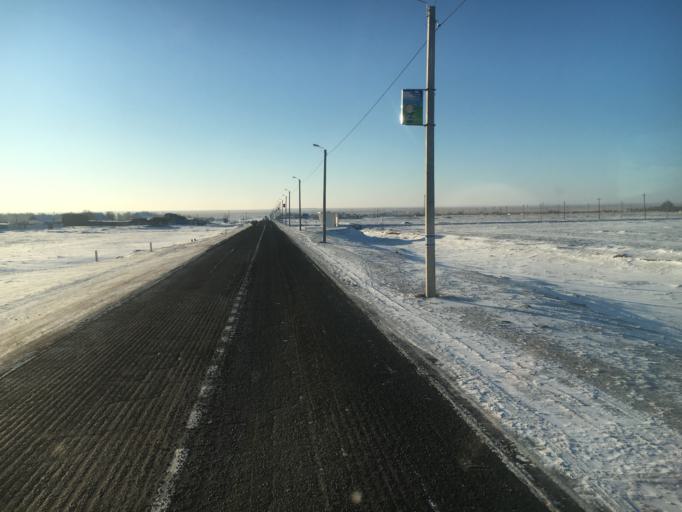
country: KZ
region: Aqtoebe
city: Khromtau
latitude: 50.1265
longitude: 59.1096
